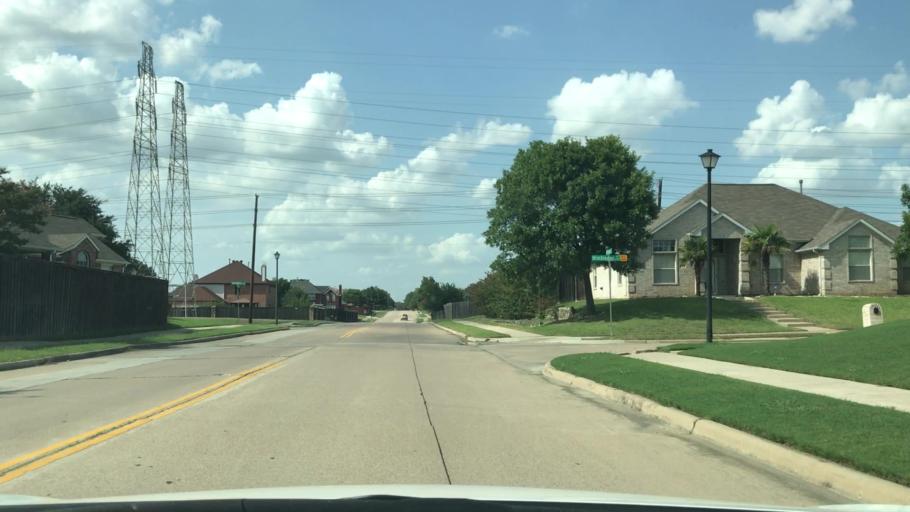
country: US
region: Texas
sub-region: Dallas County
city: Carrollton
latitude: 32.9756
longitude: -96.8643
